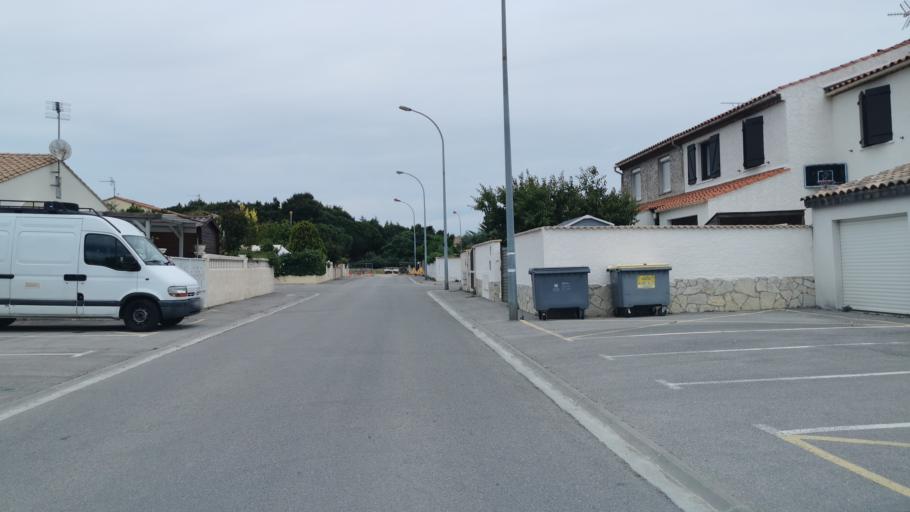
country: FR
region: Languedoc-Roussillon
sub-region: Departement de l'Aude
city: Narbonne
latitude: 43.1893
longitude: 3.0277
